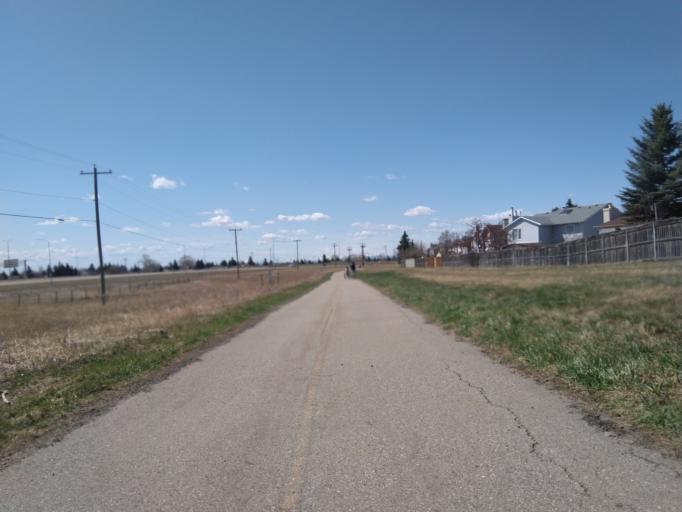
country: CA
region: Alberta
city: Chestermere
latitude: 51.0692
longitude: -113.9262
